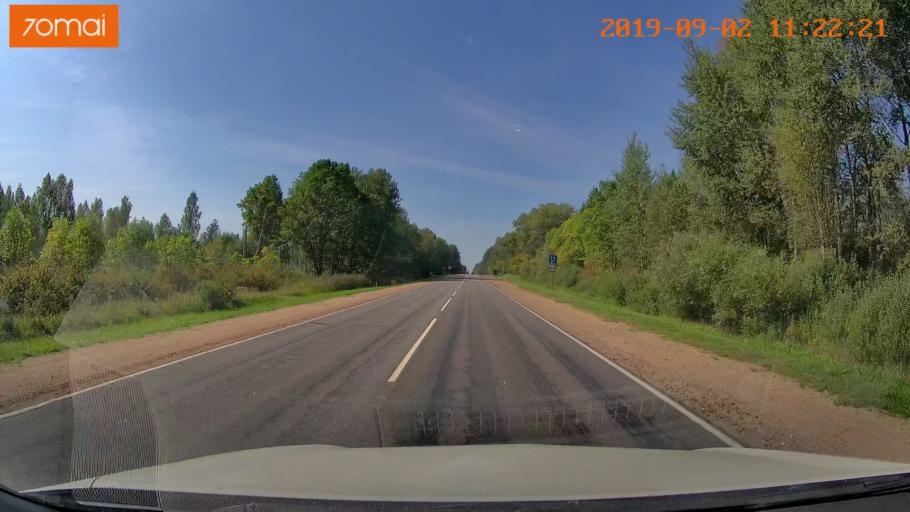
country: RU
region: Smolensk
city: Roslavl'
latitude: 54.0268
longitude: 33.0159
